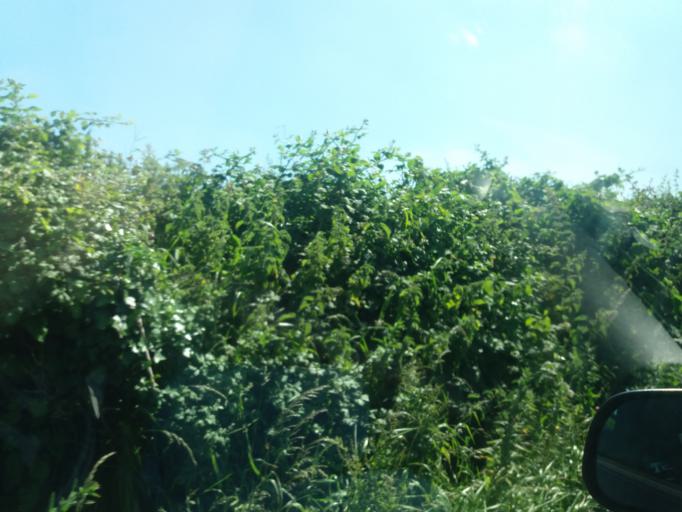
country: IE
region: Leinster
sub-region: An Mhi
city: Stamullin
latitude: 53.5898
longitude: -6.2802
